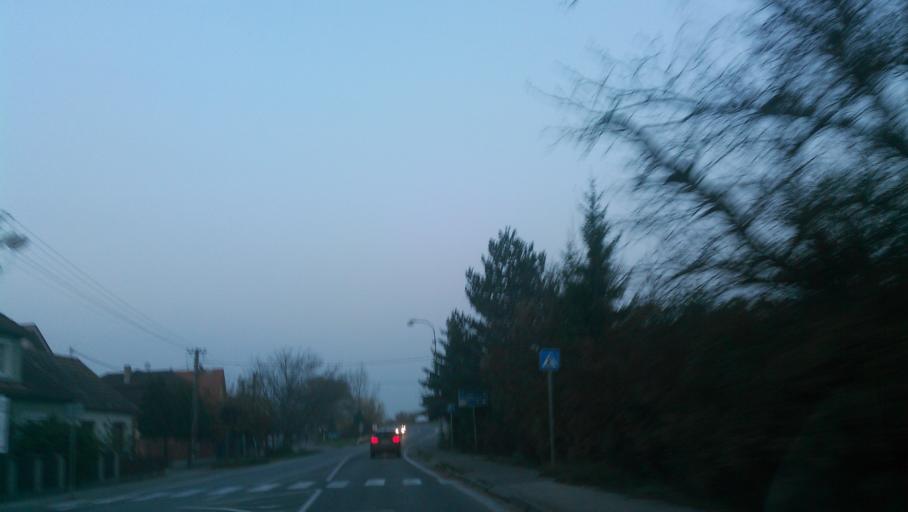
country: SK
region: Bratislavsky
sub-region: Okres Pezinok
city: Pezinok
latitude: 48.2880
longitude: 17.2765
